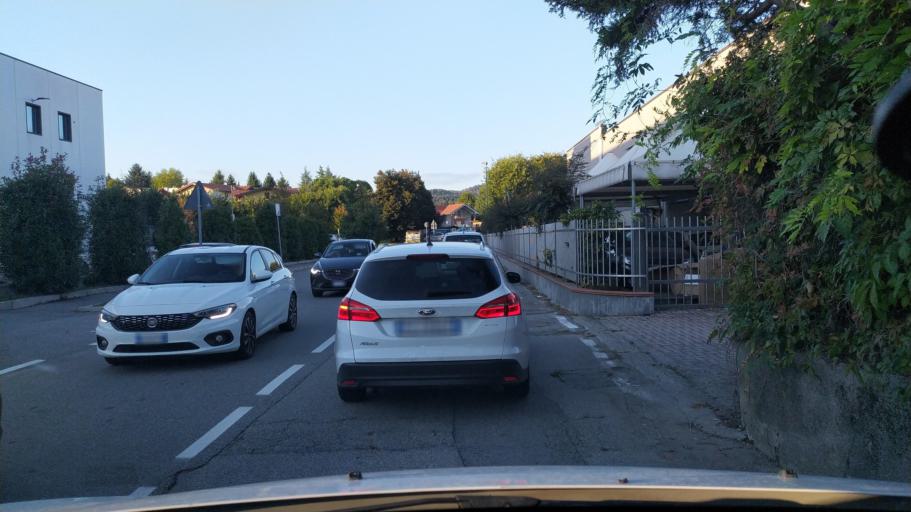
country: IT
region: Lombardy
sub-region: Provincia di Varese
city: Sesto Calende
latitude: 45.7262
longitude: 8.6502
